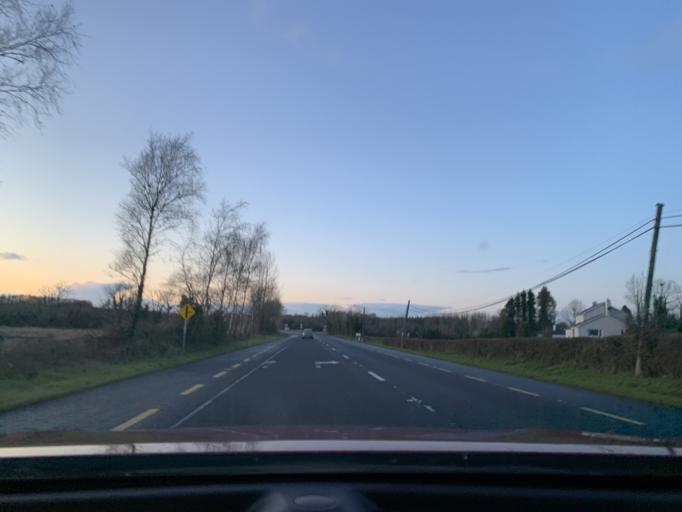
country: IE
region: Connaught
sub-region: County Leitrim
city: Carrick-on-Shannon
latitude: 53.9155
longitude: -7.9743
